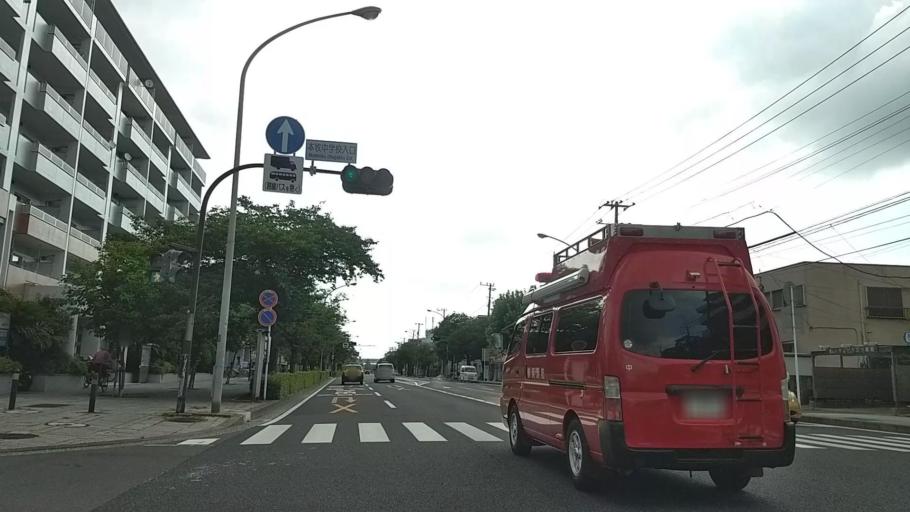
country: JP
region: Kanagawa
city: Yokohama
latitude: 35.4209
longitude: 139.6567
